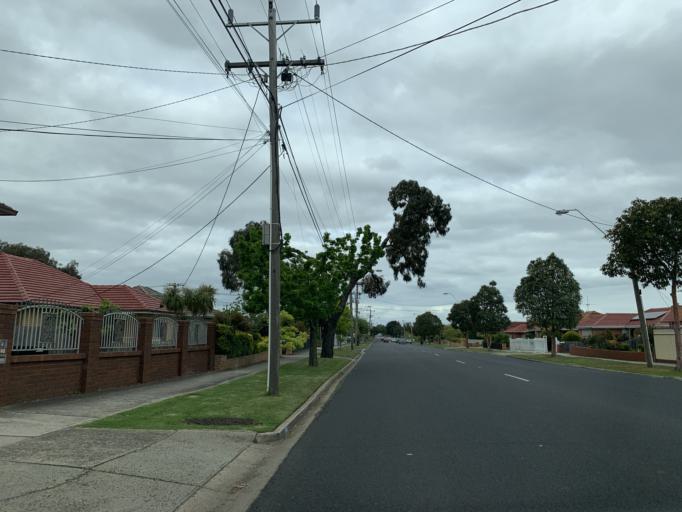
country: AU
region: Victoria
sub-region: Brimbank
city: St Albans
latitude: -37.7459
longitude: 144.8137
